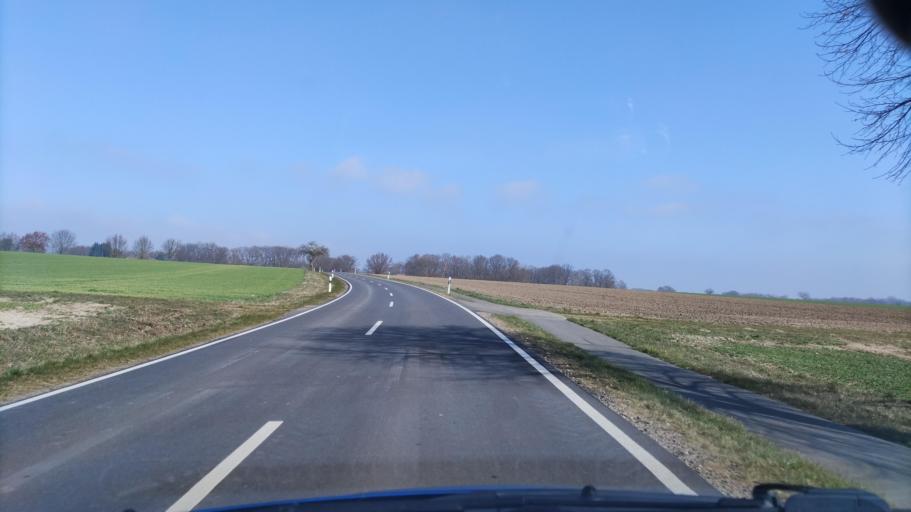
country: DE
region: Lower Saxony
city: Clenze
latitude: 52.9597
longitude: 10.9732
